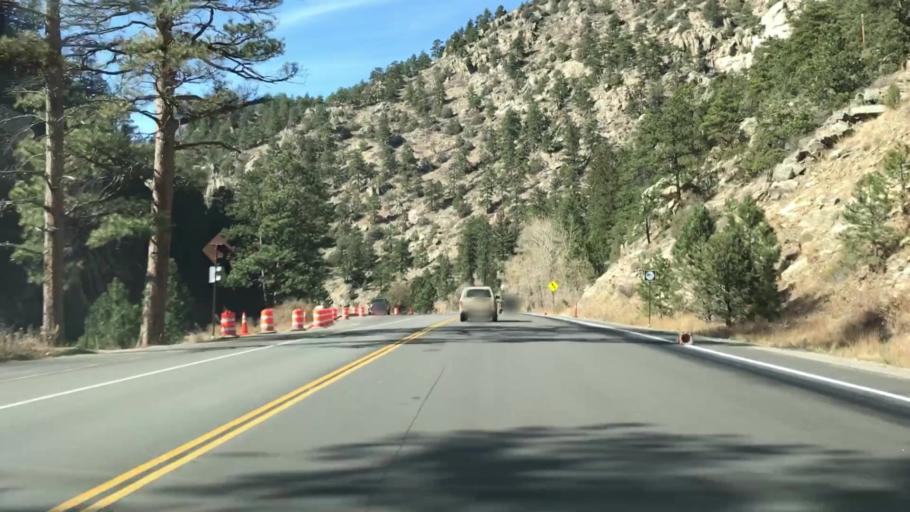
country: US
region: Colorado
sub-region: Larimer County
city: Estes Park
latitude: 40.4100
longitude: -105.3866
